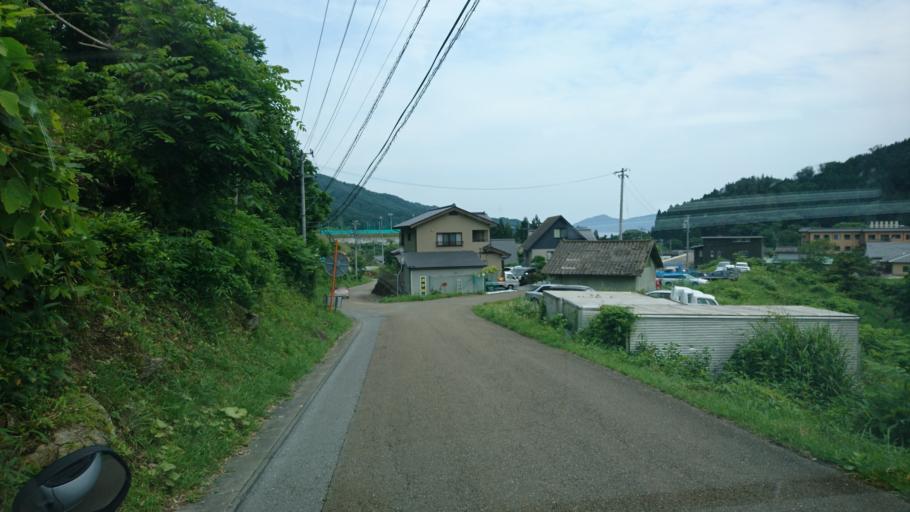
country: JP
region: Iwate
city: Ofunato
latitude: 39.1272
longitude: 141.8054
